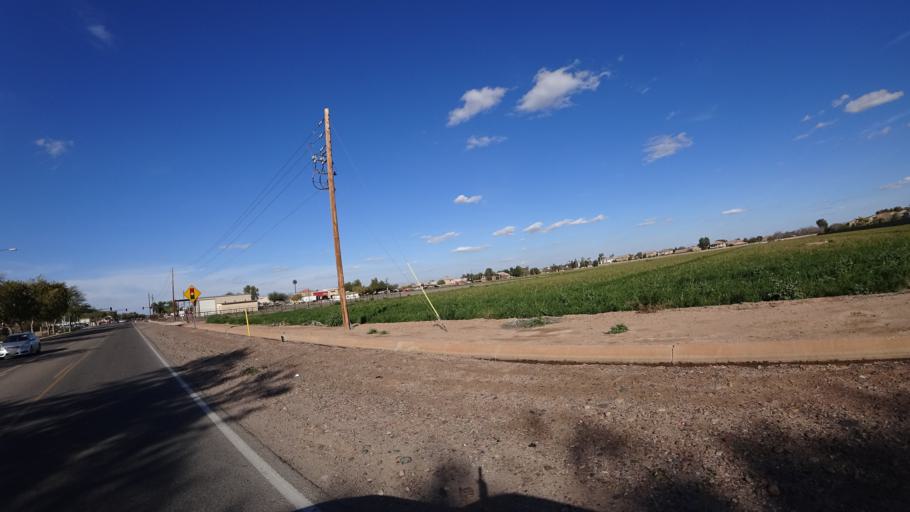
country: US
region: Arizona
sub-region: Maricopa County
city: Tolleson
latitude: 33.4210
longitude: -112.2385
